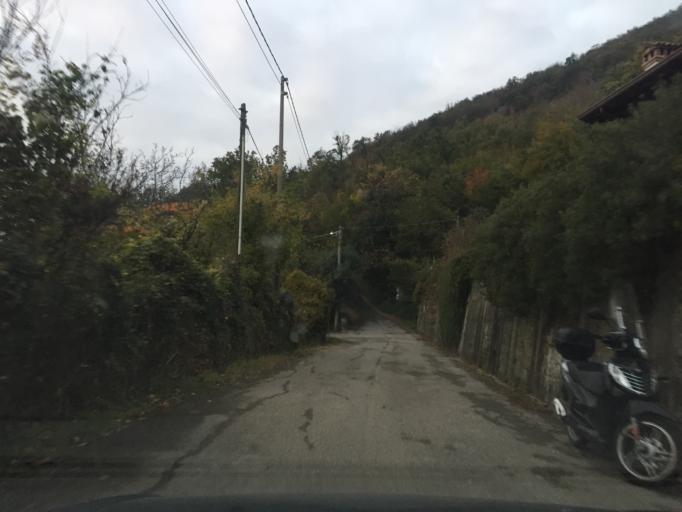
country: SI
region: Nova Gorica
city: Solkan
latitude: 45.9809
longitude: 13.6314
